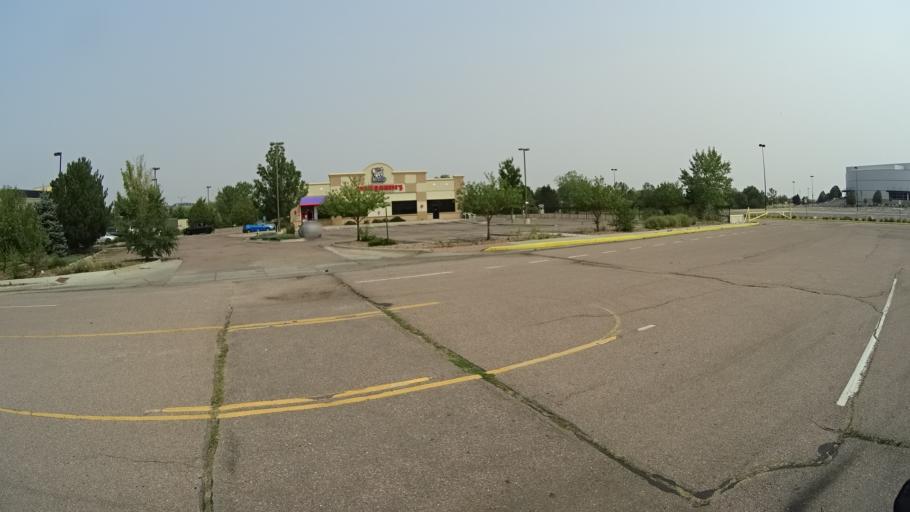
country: US
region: Colorado
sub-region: El Paso County
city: Stratmoor
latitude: 38.7902
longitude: -104.7964
